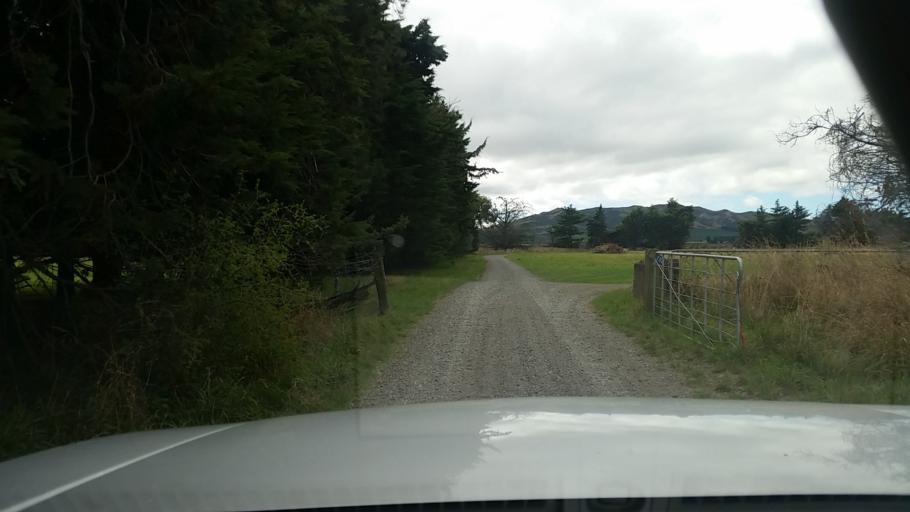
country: NZ
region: Marlborough
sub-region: Marlborough District
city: Blenheim
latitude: -41.6710
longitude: 174.0386
